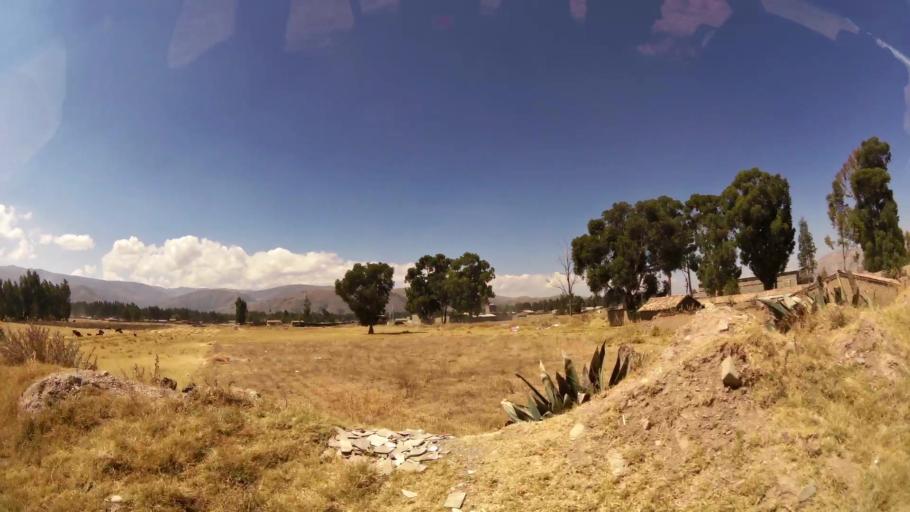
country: PE
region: Junin
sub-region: Provincia de Jauja
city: Jauja
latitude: -11.7664
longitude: -75.4968
